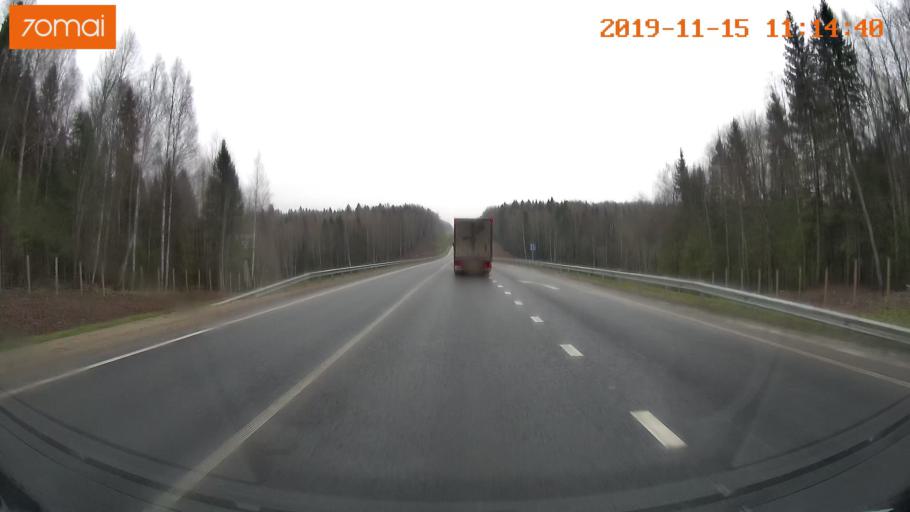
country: RU
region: Vologda
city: Chebsara
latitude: 59.1255
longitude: 39.1934
